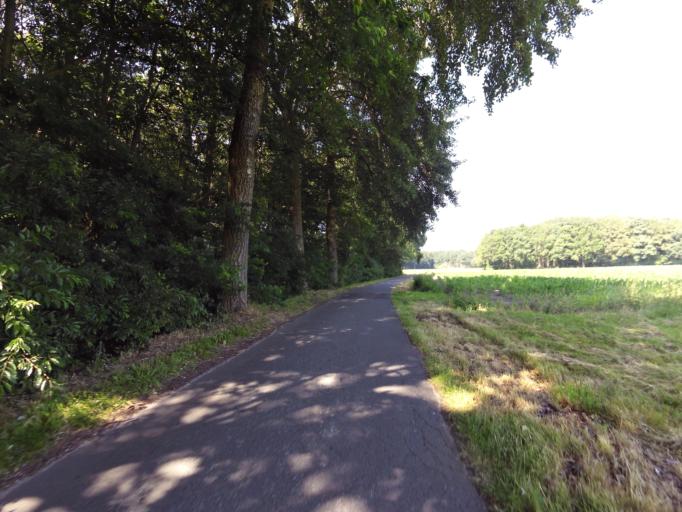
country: BE
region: Flanders
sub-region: Provincie West-Vlaanderen
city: Zedelgem
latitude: 51.1555
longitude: 3.1409
